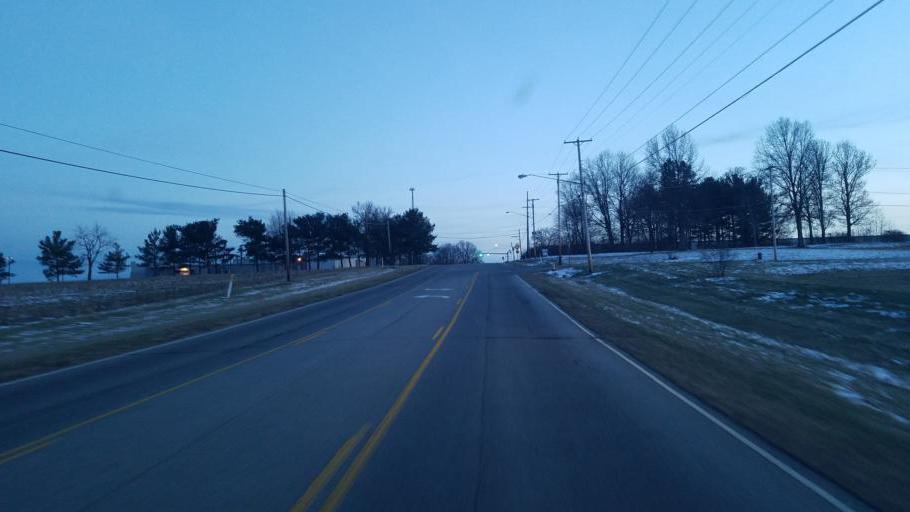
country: US
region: Ohio
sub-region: Ashland County
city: Ashland
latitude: 40.8591
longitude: -82.2792
